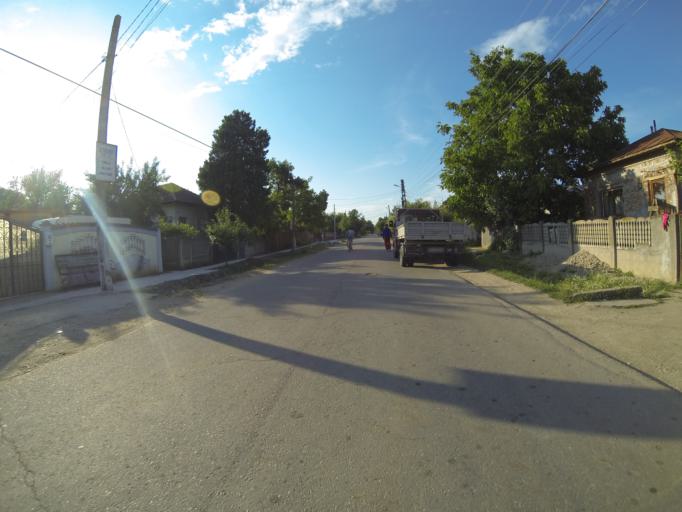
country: RO
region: Dolj
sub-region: Comuna Podari
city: Podari
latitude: 44.2135
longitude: 23.7928
